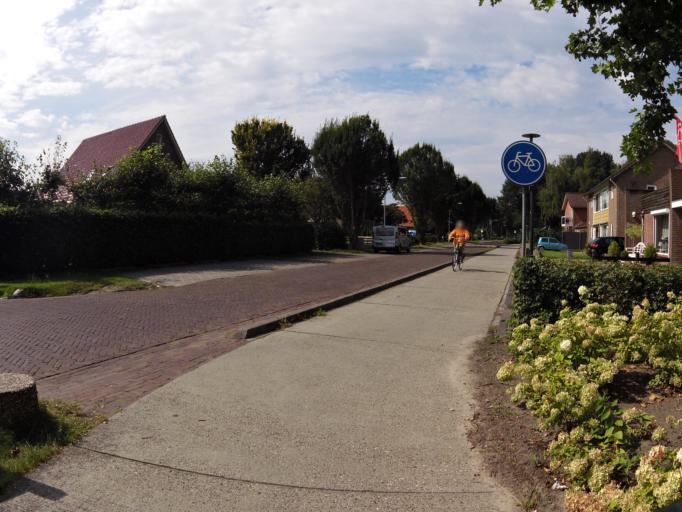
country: NL
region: Drenthe
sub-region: Gemeente Emmen
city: Klazienaveen
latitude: 52.6710
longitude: 6.9998
